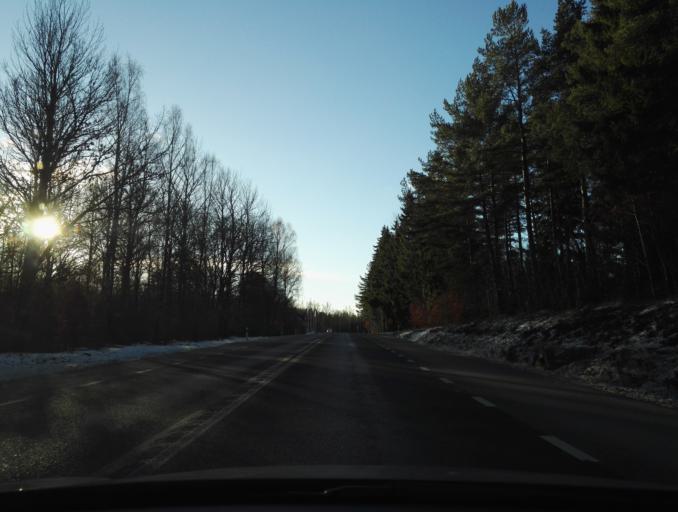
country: SE
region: Kronoberg
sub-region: Vaxjo Kommun
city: Vaexjoe
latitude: 56.8590
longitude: 14.7314
